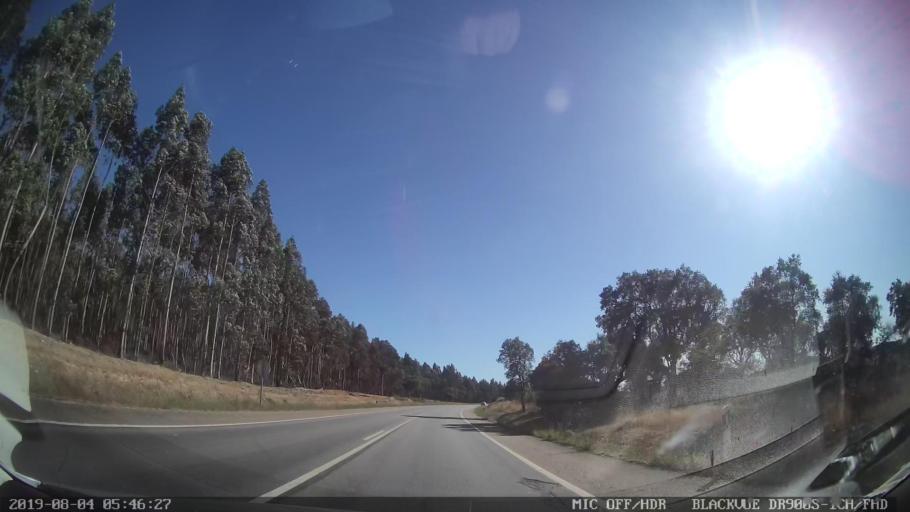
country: PT
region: Portalegre
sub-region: Gaviao
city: Gaviao
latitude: 39.4504
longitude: -7.7883
